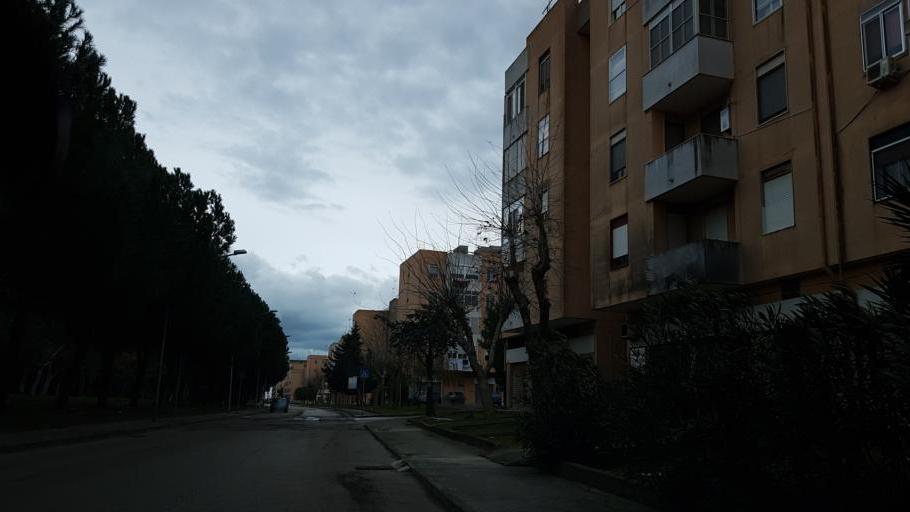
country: IT
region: Apulia
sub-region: Provincia di Brindisi
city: Brindisi
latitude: 40.6206
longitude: 17.9274
